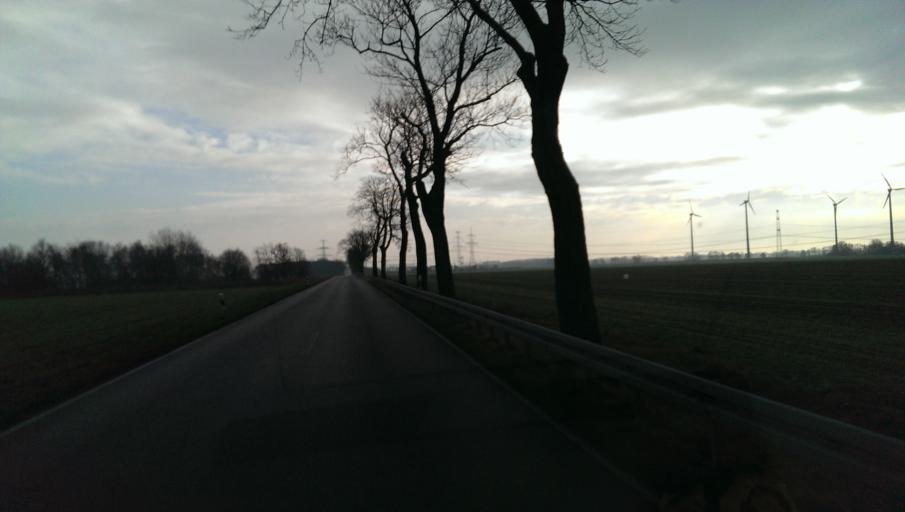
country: DE
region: Saxony-Anhalt
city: Holzdorf
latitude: 51.8353
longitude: 13.1489
